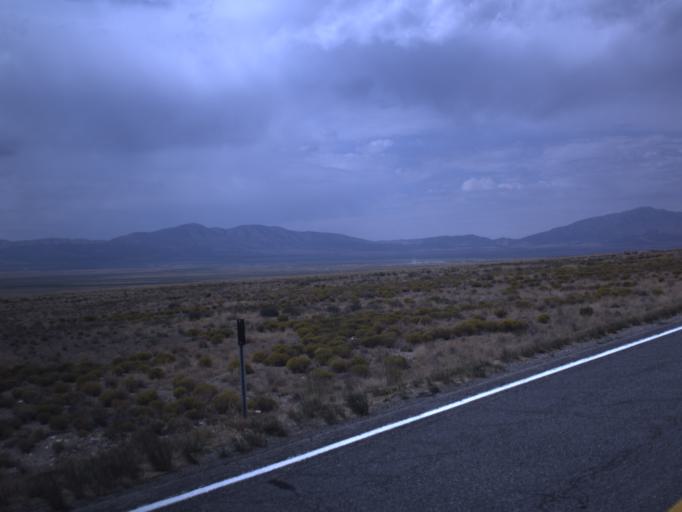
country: US
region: Utah
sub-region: Utah County
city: Eagle Mountain
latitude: 40.2553
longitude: -112.2243
